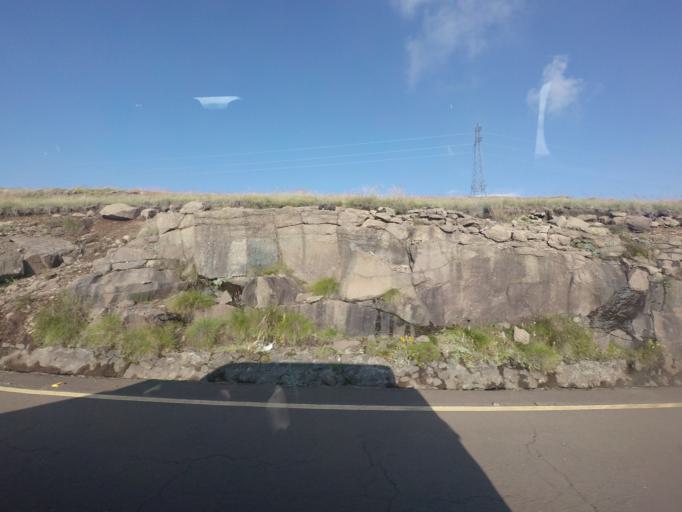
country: LS
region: Butha-Buthe
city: Butha-Buthe
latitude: -29.1006
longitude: 28.4248
